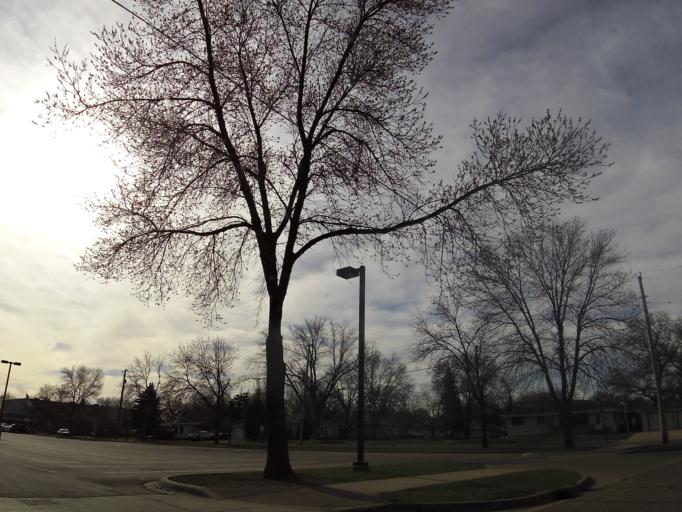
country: US
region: Minnesota
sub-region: Scott County
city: Savage
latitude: 44.7756
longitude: -93.3401
